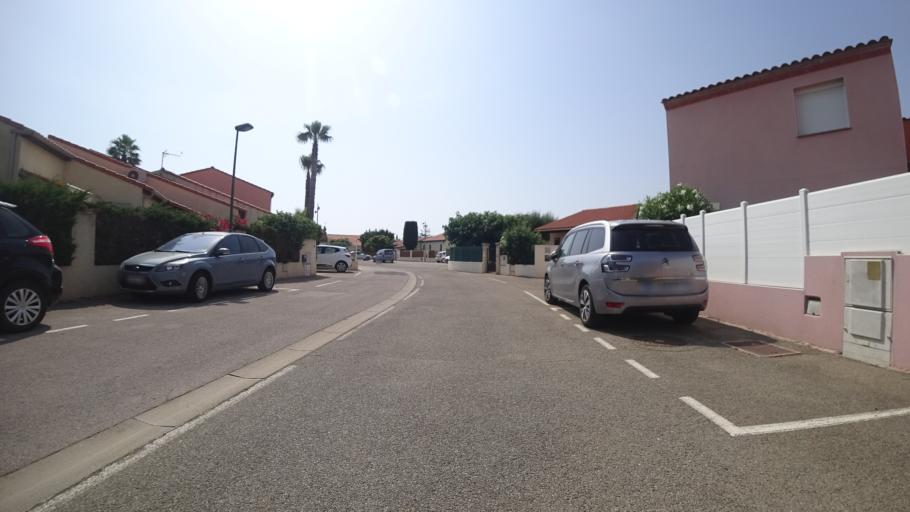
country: FR
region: Languedoc-Roussillon
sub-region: Departement des Pyrenees-Orientales
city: Saint-Laurent-de-la-Salanque
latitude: 42.7707
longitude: 3.0046
